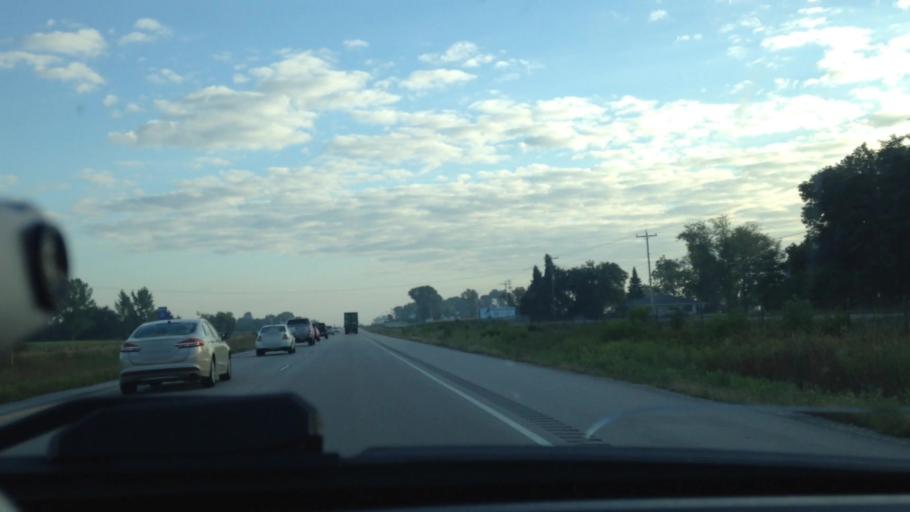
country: US
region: Wisconsin
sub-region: Brown County
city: Wrightstown
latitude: 44.3601
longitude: -88.1834
